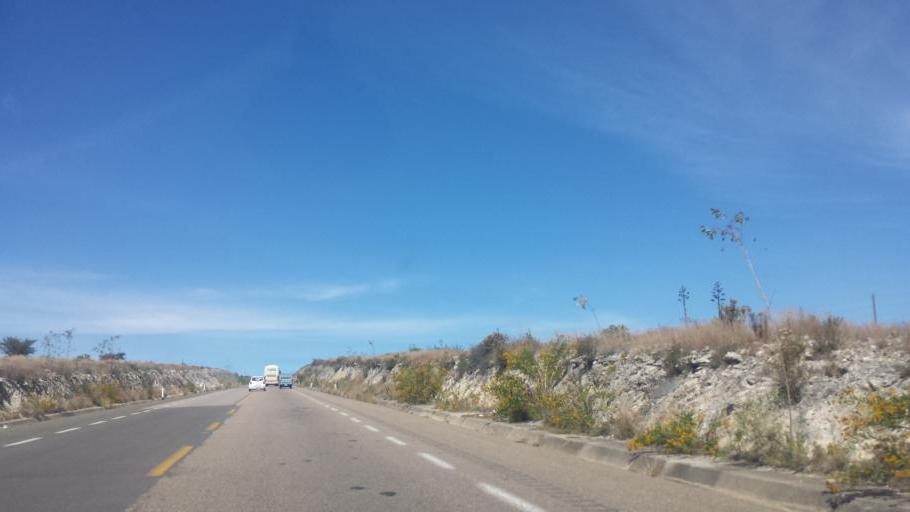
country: MX
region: Oaxaca
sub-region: Villa Tejupam de la Union
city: Villa Tejupam de la Union
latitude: 17.7692
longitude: -97.3577
